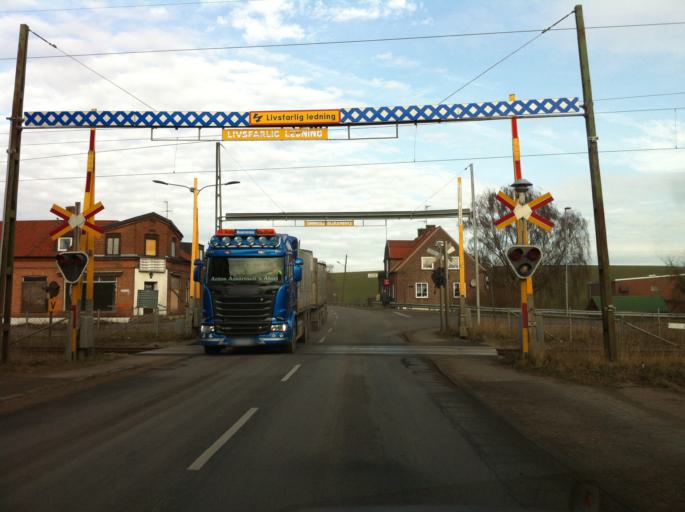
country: SE
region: Skane
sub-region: Landskrona
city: Asmundtorp
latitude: 55.9261
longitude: 12.9557
